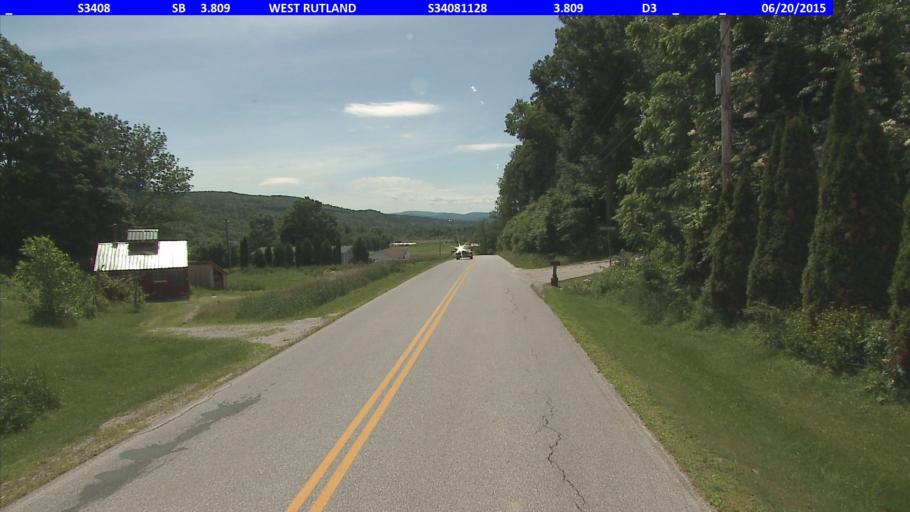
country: US
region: Vermont
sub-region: Rutland County
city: West Rutland
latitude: 43.6635
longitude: -73.0748
